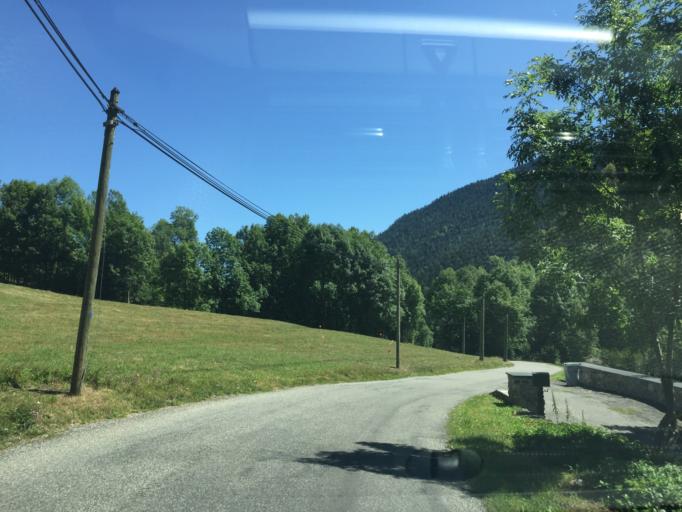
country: FR
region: Midi-Pyrenees
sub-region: Departement des Hautes-Pyrenees
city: Saint-Lary-Soulan
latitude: 42.8493
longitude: 0.3006
